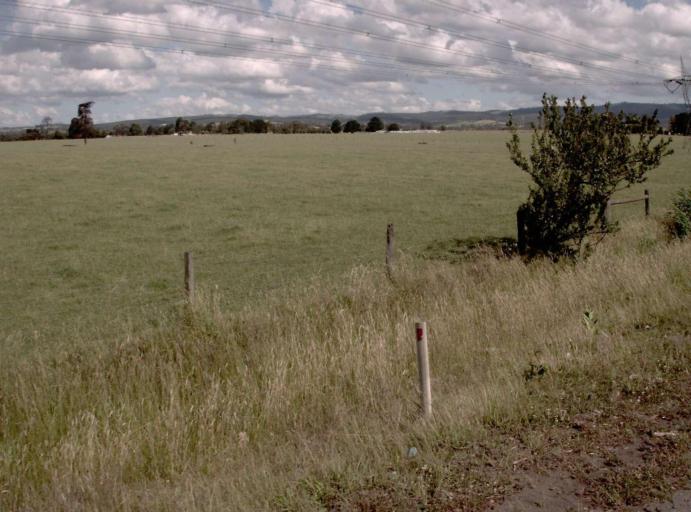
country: AU
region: Victoria
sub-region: Latrobe
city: Morwell
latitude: -38.2623
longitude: 146.4345
